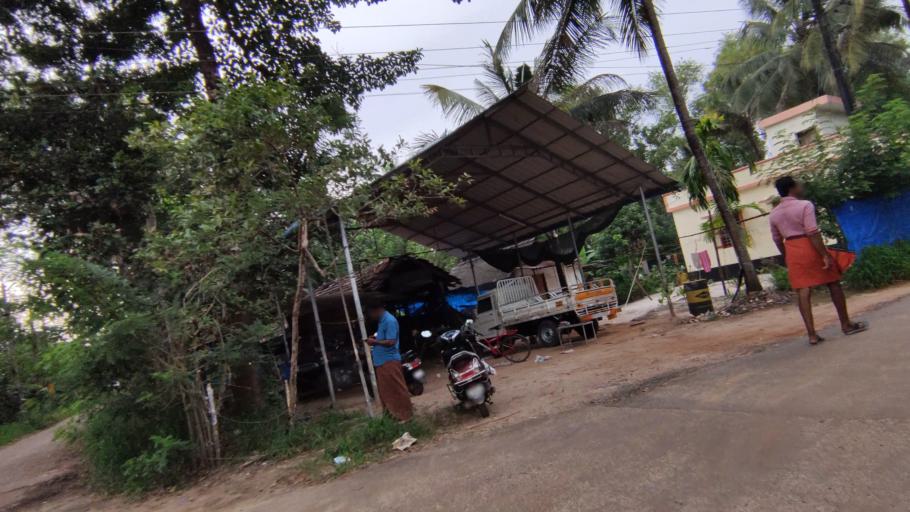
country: IN
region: Kerala
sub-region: Alappuzha
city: Shertallai
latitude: 9.6290
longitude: 76.3578
